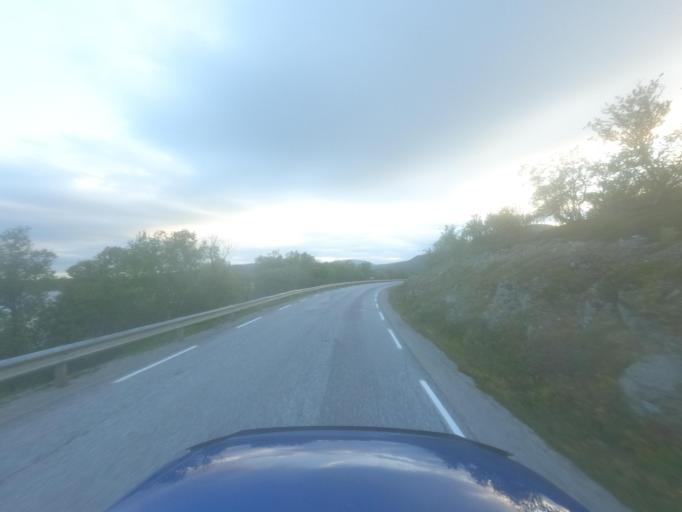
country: NO
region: Finnmark Fylke
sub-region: Porsanger
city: Lakselv
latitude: 70.3648
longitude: 25.0720
